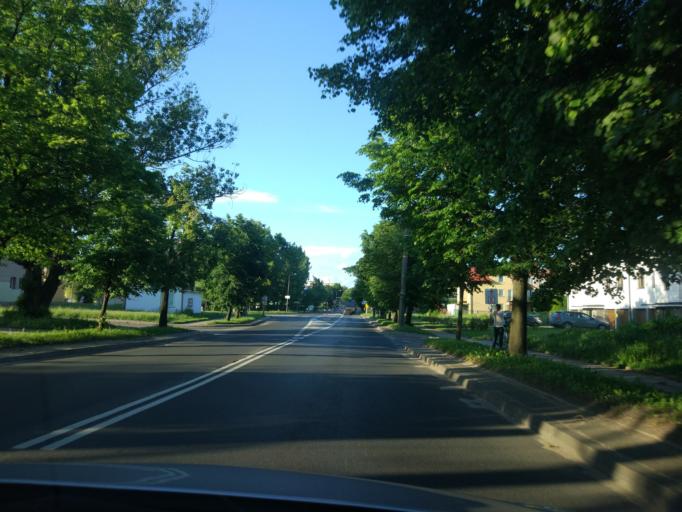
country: PL
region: Lodz Voivodeship
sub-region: Powiat kutnowski
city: Kutno
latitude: 52.2255
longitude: 19.3643
